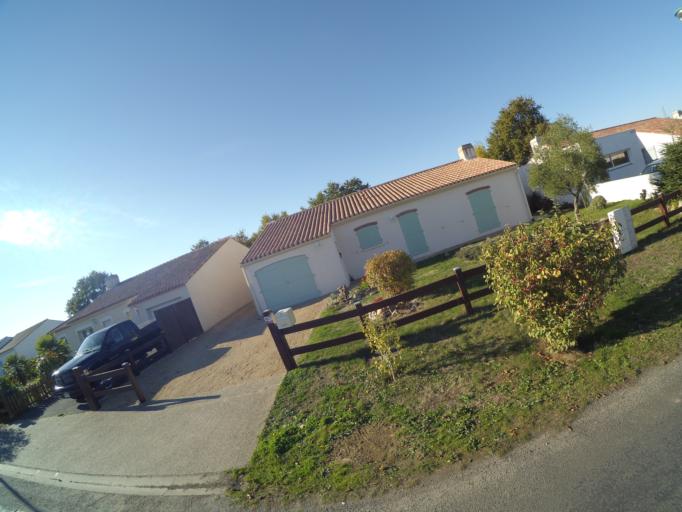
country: FR
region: Pays de la Loire
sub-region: Departement de la Loire-Atlantique
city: Saint-Lumine-de-Clisson
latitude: 47.0862
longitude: -1.3398
